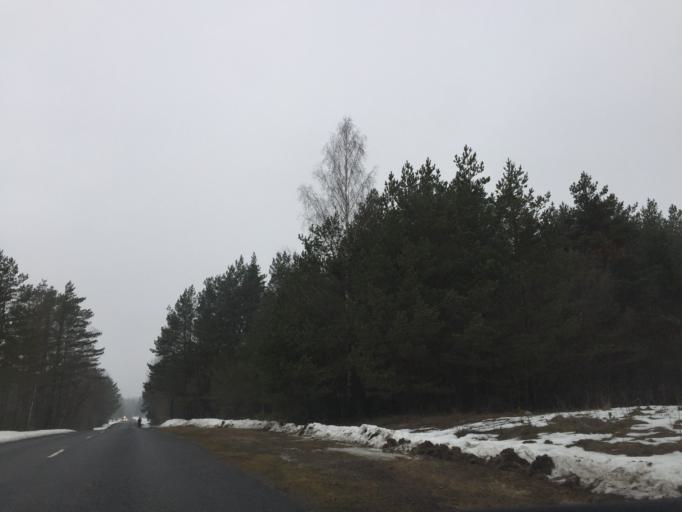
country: EE
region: Saare
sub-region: Orissaare vald
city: Orissaare
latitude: 58.4036
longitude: 22.8001
